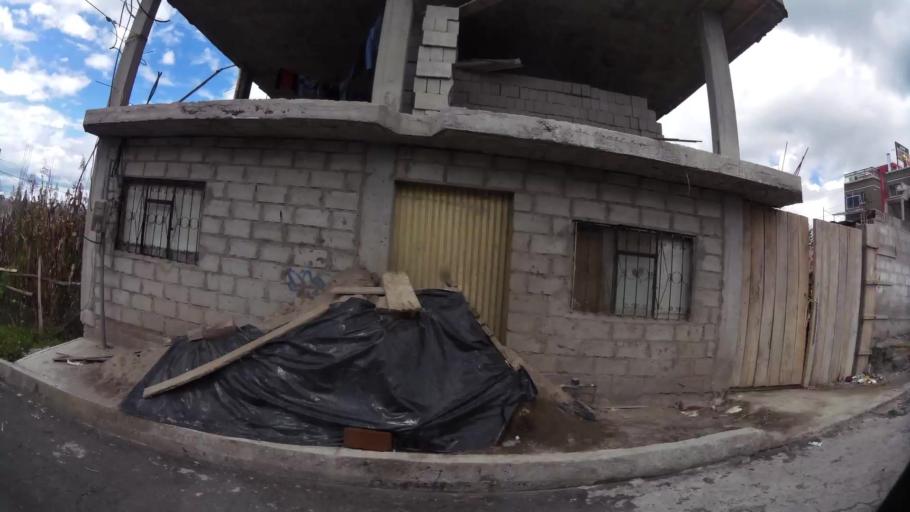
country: EC
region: Pichincha
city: Sangolqui
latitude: -0.3434
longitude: -78.5591
